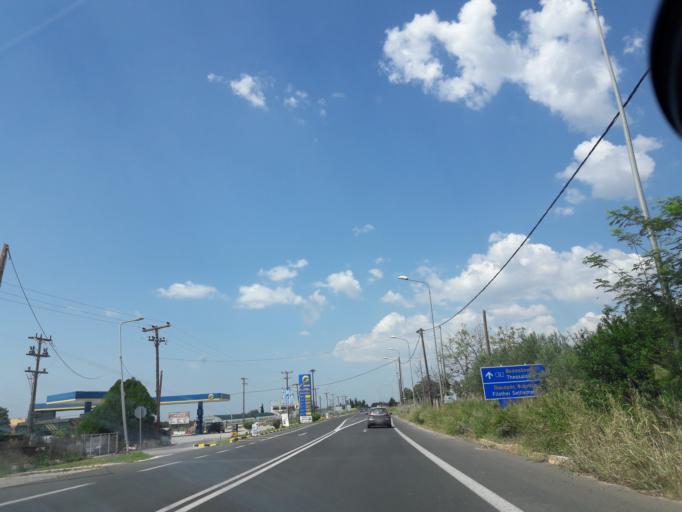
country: GR
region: Central Macedonia
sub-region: Nomos Thessalonikis
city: Agia Paraskevi
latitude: 40.5168
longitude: 23.0674
